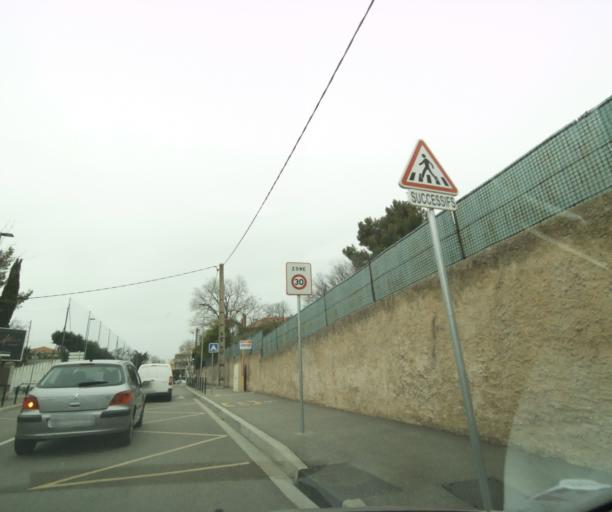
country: FR
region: Provence-Alpes-Cote d'Azur
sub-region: Departement des Bouches-du-Rhone
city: Aix-en-Provence
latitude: 43.5202
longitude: 5.4558
